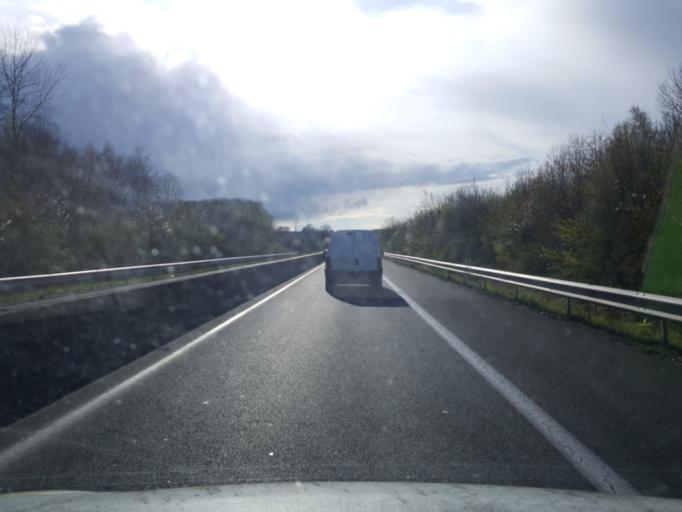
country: FR
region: Picardie
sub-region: Departement de l'Oise
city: Goincourt
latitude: 49.3842
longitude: 2.0483
